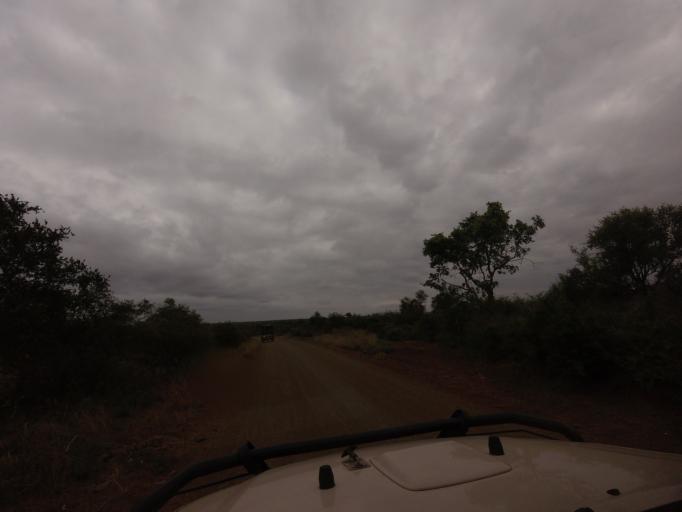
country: ZA
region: Mpumalanga
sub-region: Ehlanzeni District
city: Komatipoort
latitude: -25.1660
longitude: 31.9385
